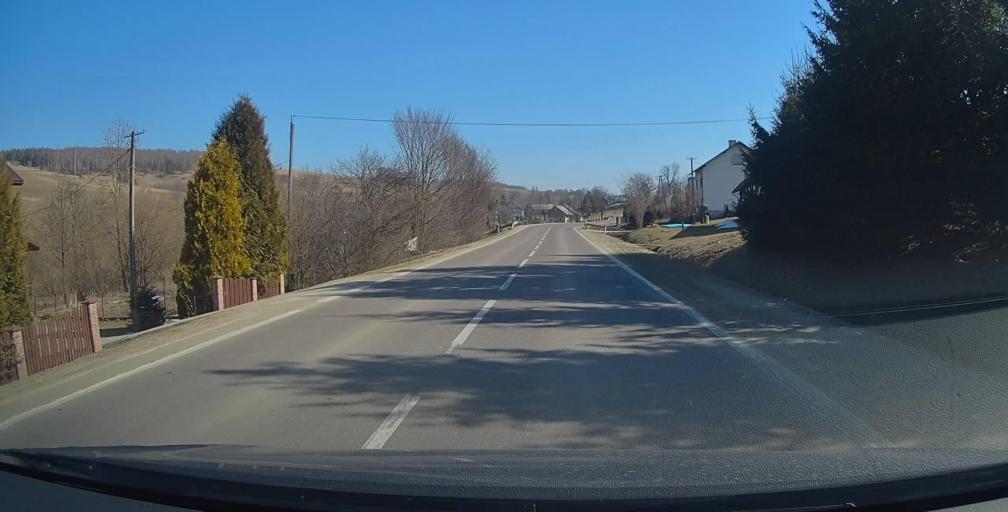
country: PL
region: Subcarpathian Voivodeship
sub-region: Powiat sanocki
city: Tyrawa Woloska
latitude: 49.6136
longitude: 22.4336
